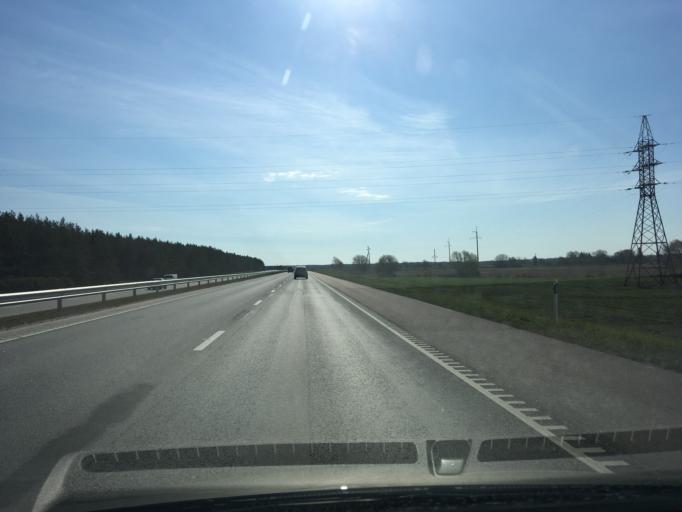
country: EE
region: Harju
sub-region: Raasiku vald
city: Arukula
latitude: 59.4450
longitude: 25.1053
